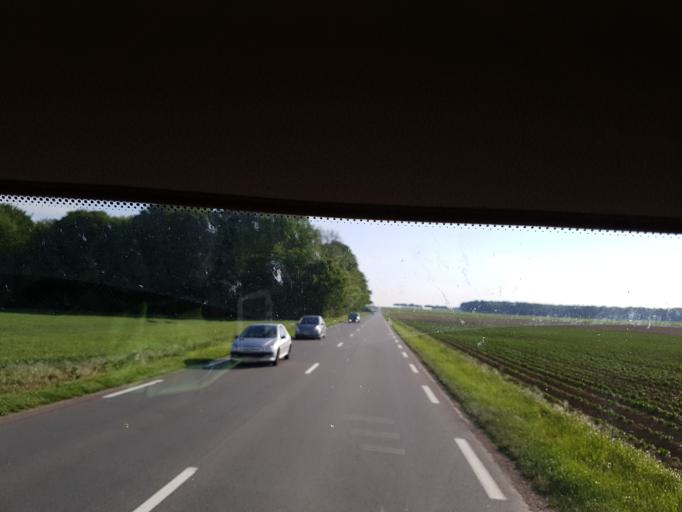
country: FR
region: Picardie
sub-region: Departement de la Somme
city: Crecy-en-Ponthieu
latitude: 50.2186
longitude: 1.9185
